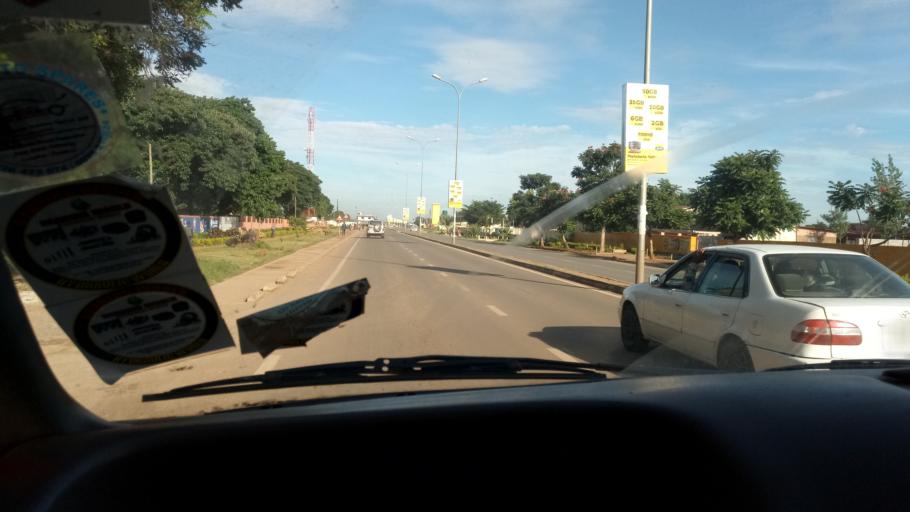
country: ZM
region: Lusaka
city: Lusaka
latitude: -15.4423
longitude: 28.3146
